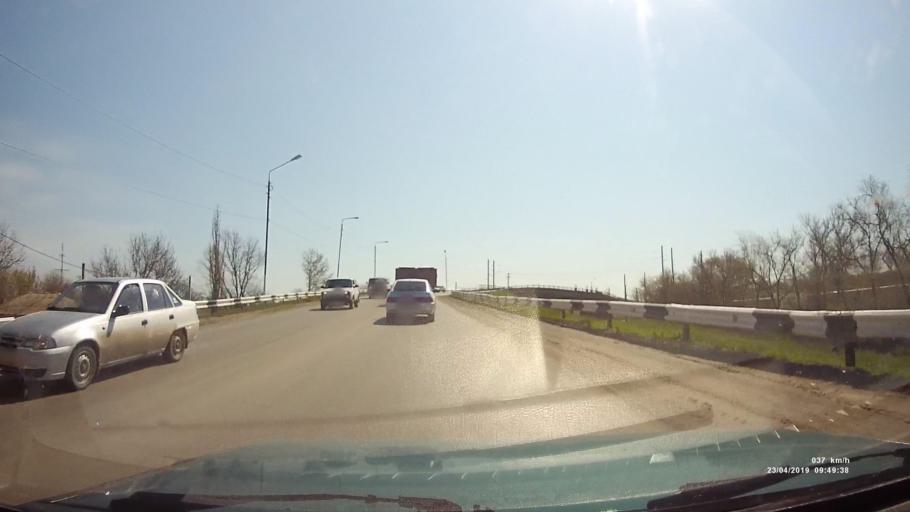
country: RU
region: Rostov
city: Orlovskiy
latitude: 46.8647
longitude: 42.0345
